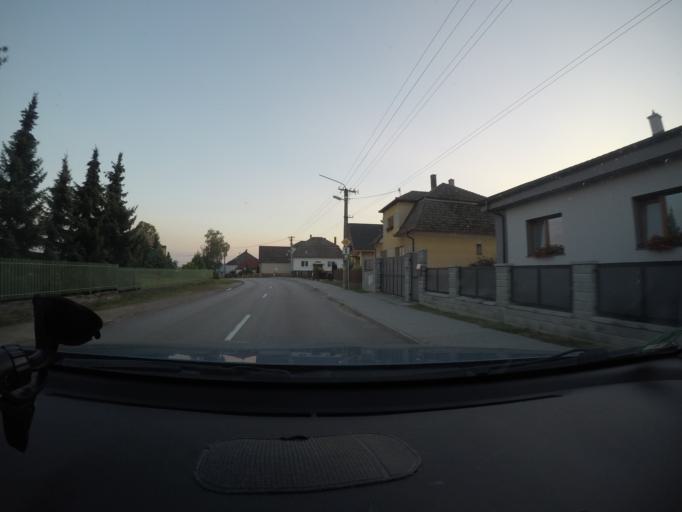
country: SK
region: Trenciansky
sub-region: Okres Nove Mesto nad Vahom
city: Nove Mesto nad Vahom
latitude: 48.8453
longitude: 17.9139
